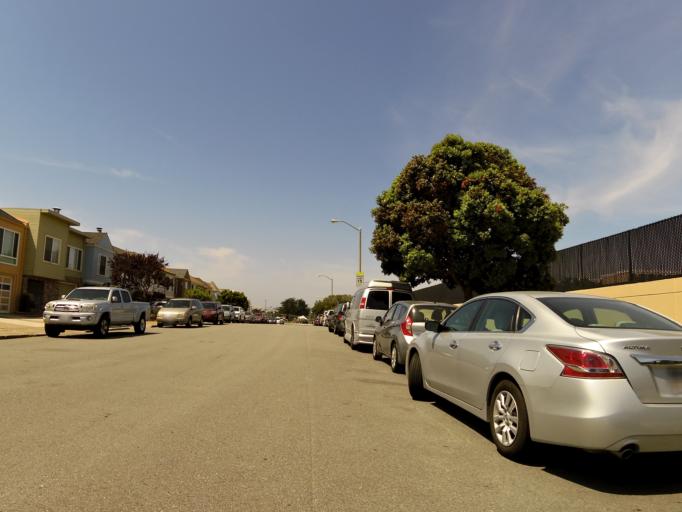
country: US
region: California
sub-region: San Mateo County
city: Daly City
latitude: 37.7464
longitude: -122.4974
